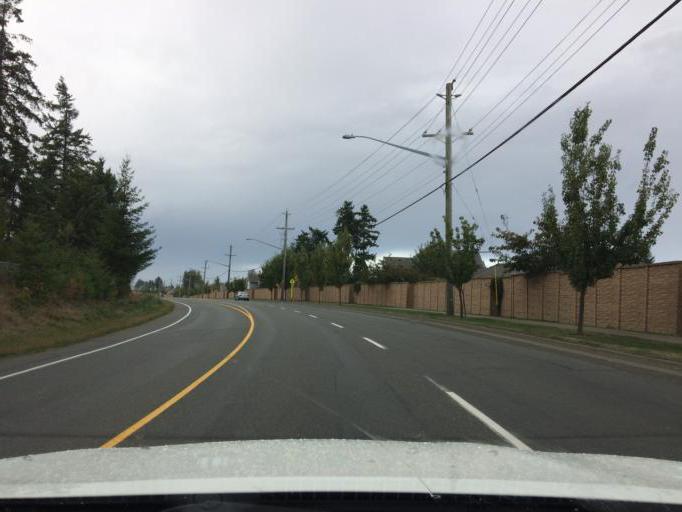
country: CA
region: British Columbia
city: Courtenay
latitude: 49.7020
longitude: -124.9556
